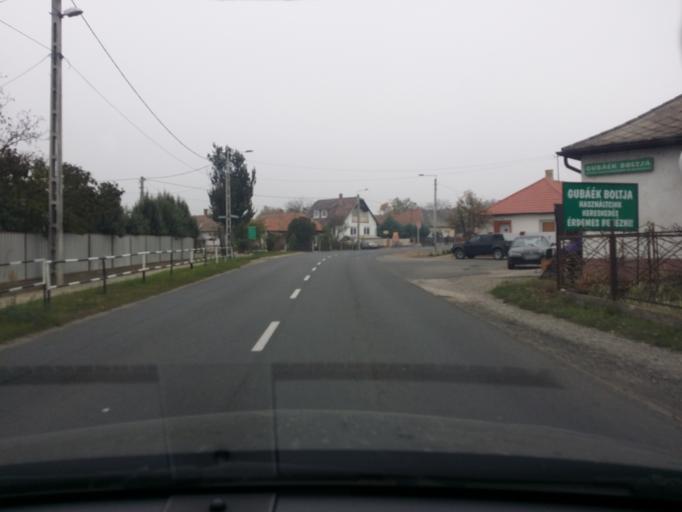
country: HU
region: Szabolcs-Szatmar-Bereg
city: Nyirpazony
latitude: 48.0132
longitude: 21.8312
